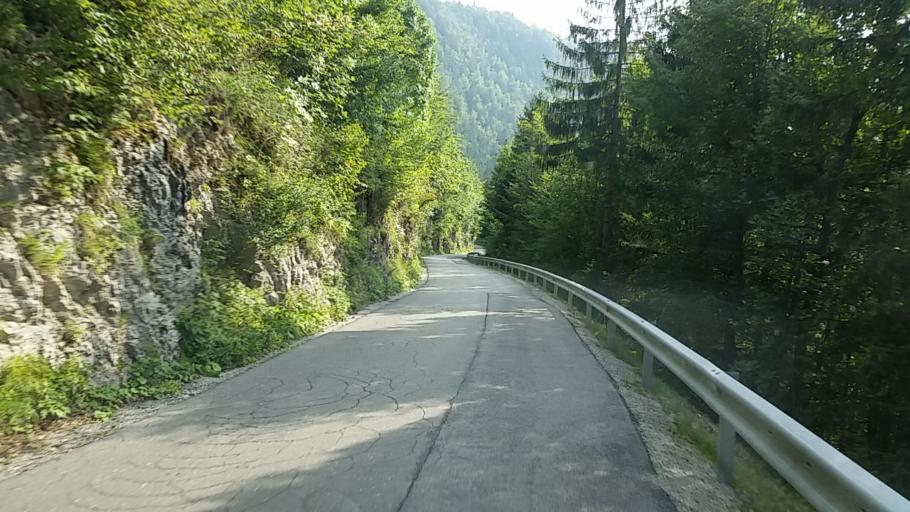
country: SI
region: Bohinj
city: Bohinjska Bistrica
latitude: 46.2718
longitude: 14.0042
